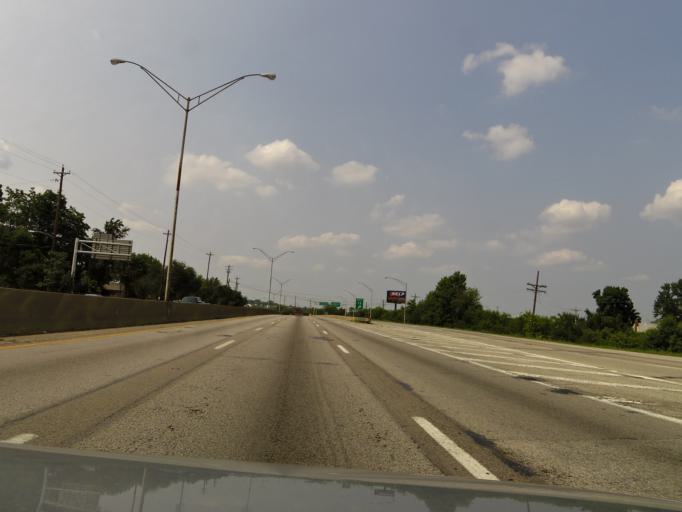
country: US
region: Ohio
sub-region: Hamilton County
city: Lockland
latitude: 39.2313
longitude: -84.4502
